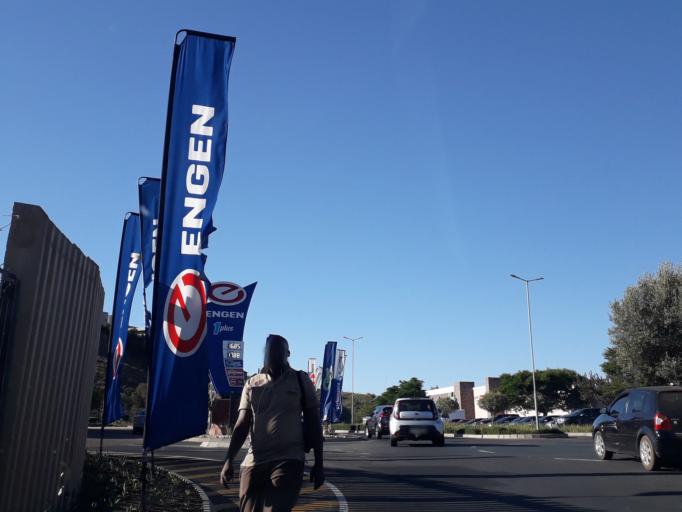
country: ZA
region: Gauteng
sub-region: City of Johannesburg Metropolitan Municipality
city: Roodepoort
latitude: -26.1496
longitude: 27.9213
